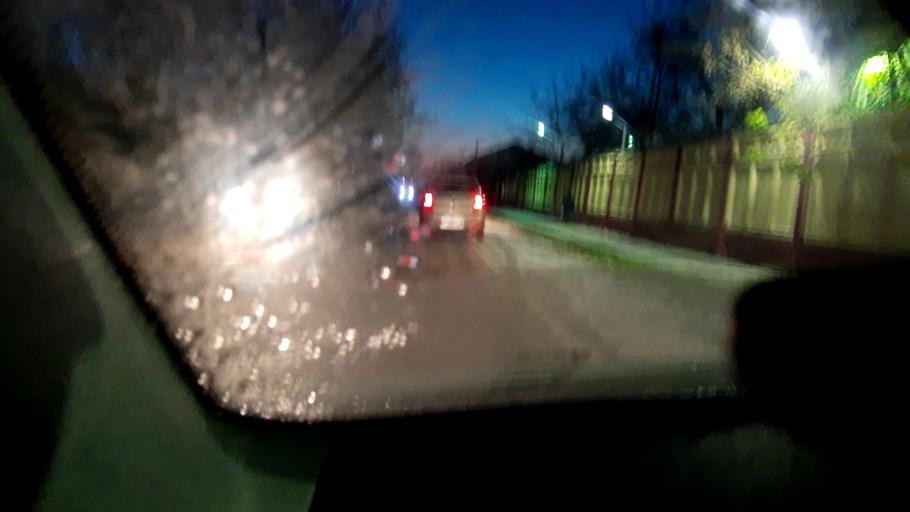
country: RU
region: Bashkortostan
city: Ufa
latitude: 54.7983
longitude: 56.0957
